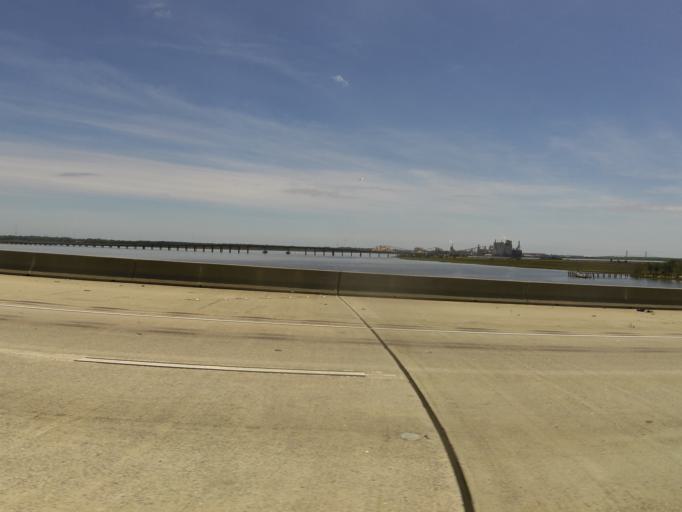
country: US
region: Georgia
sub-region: Glynn County
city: Dock Junction
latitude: 31.1889
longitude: -81.5412
